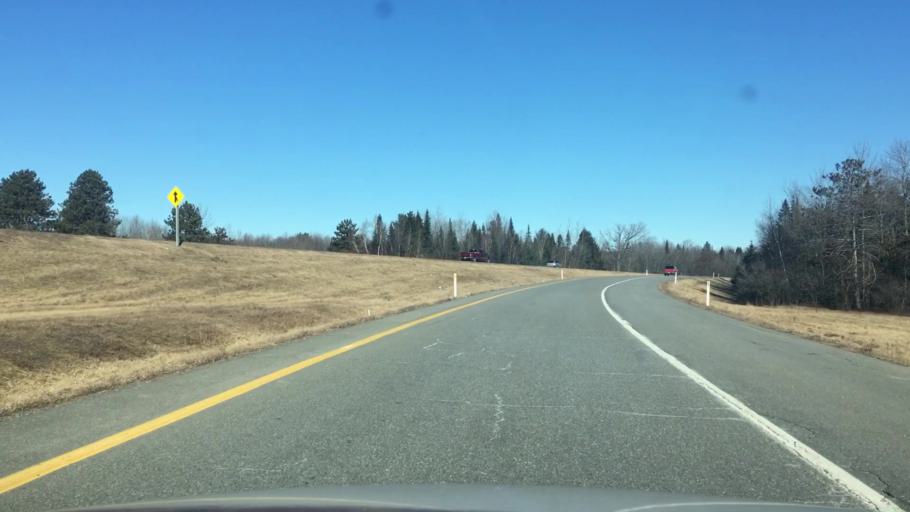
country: US
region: Maine
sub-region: Kennebec County
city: Clinton
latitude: 44.6401
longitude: -69.5261
